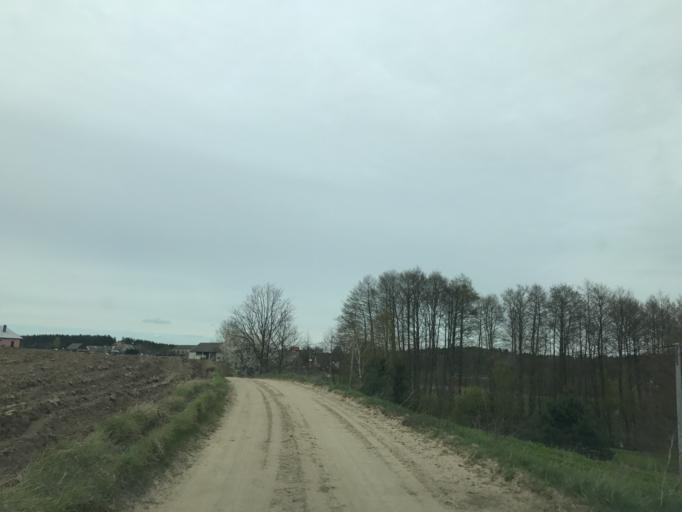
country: PL
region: Warmian-Masurian Voivodeship
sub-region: Powiat dzialdowski
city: Rybno
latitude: 53.3424
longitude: 19.8661
